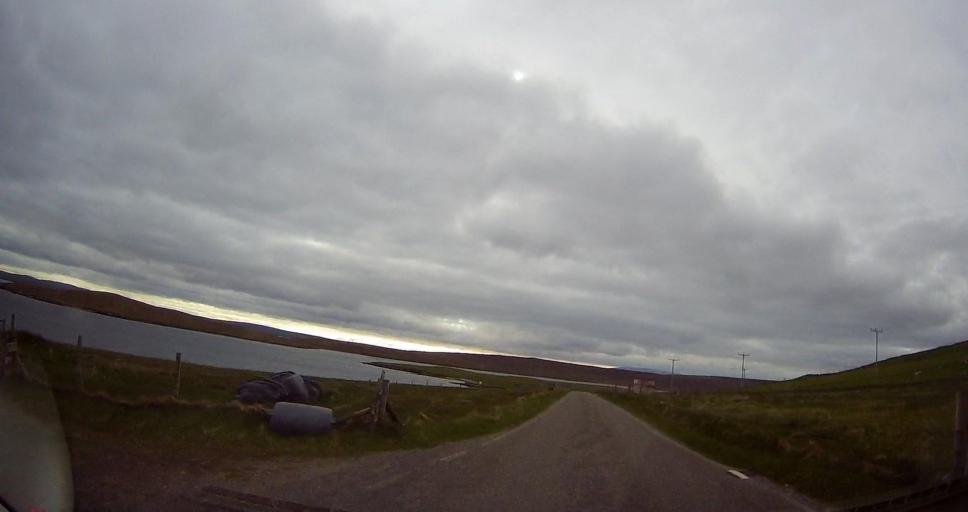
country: GB
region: Scotland
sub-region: Shetland Islands
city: Shetland
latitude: 60.4984
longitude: -1.0812
